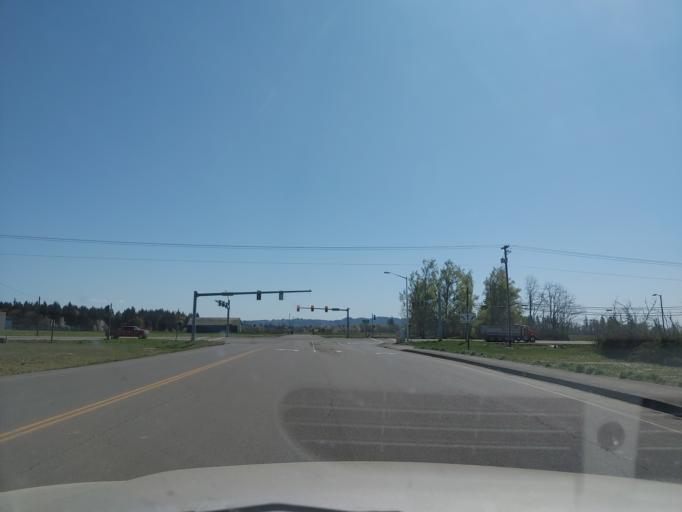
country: US
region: Oregon
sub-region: Yamhill County
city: McMinnville
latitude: 45.2018
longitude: -123.1524
